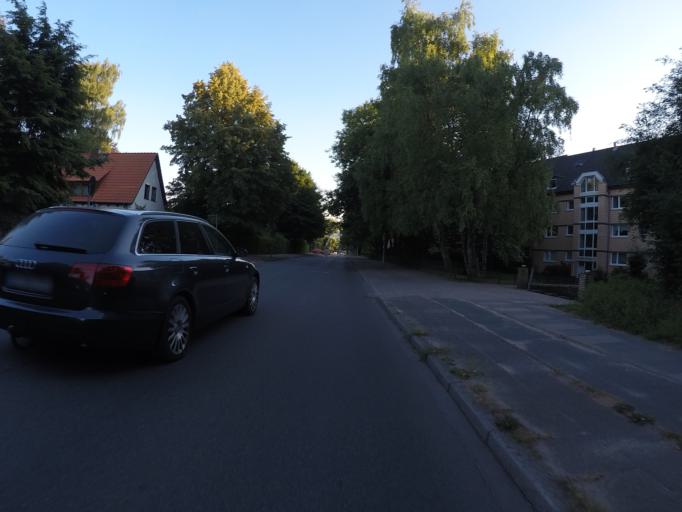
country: DE
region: Hamburg
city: Poppenbuettel
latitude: 53.6588
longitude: 10.0953
